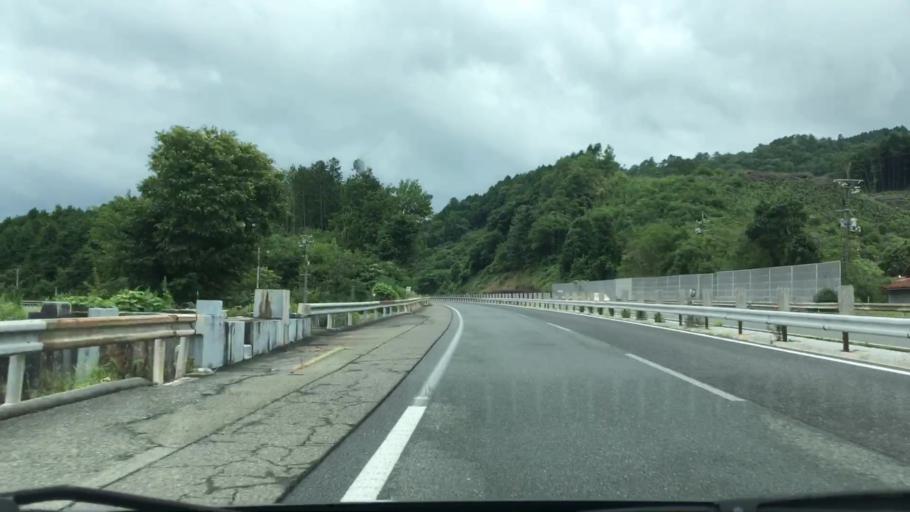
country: JP
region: Okayama
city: Niimi
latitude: 34.9408
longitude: 133.3281
